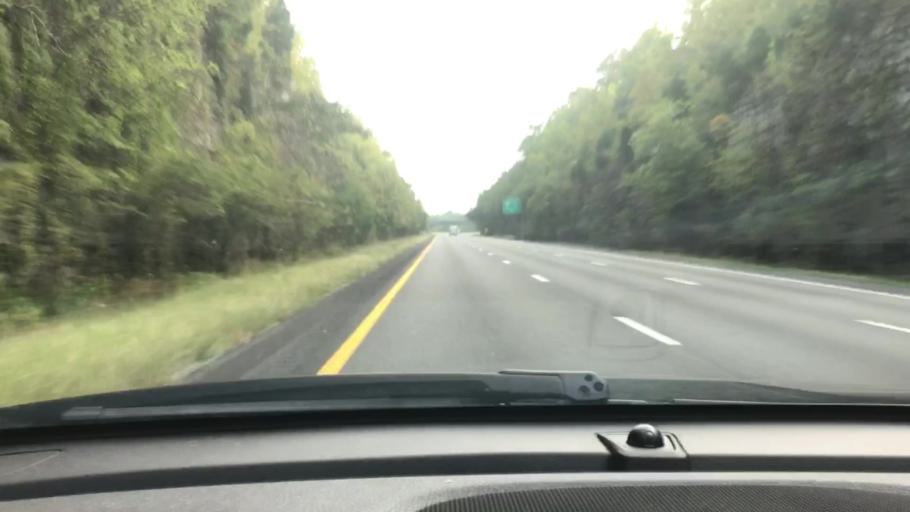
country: US
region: Tennessee
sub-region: Sumner County
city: Millersville
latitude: 36.4139
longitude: -86.7200
